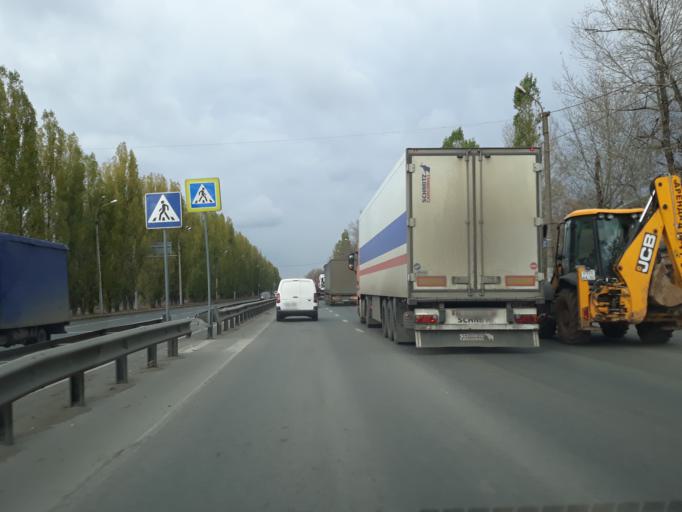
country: RU
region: Nizjnij Novgorod
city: Nizhniy Novgorod
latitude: 56.2716
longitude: 43.9098
